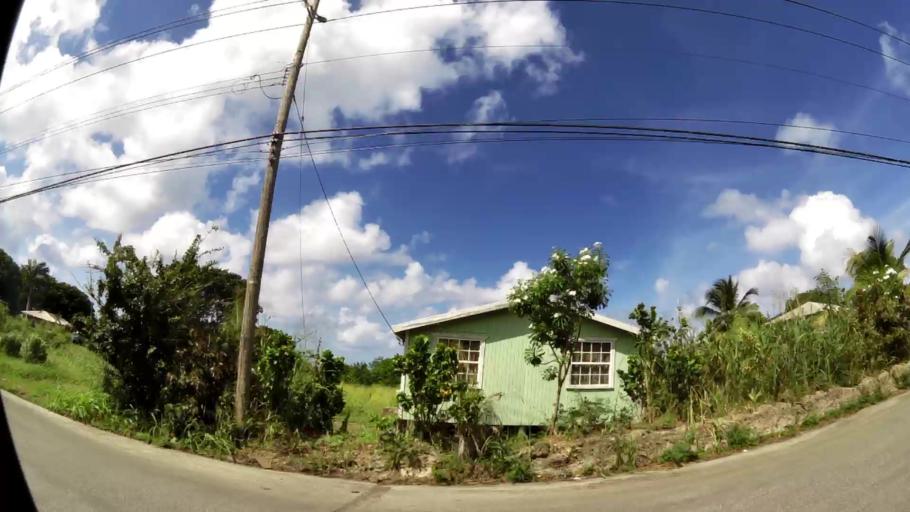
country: BB
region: Saint James
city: Holetown
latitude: 13.2033
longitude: -59.6340
